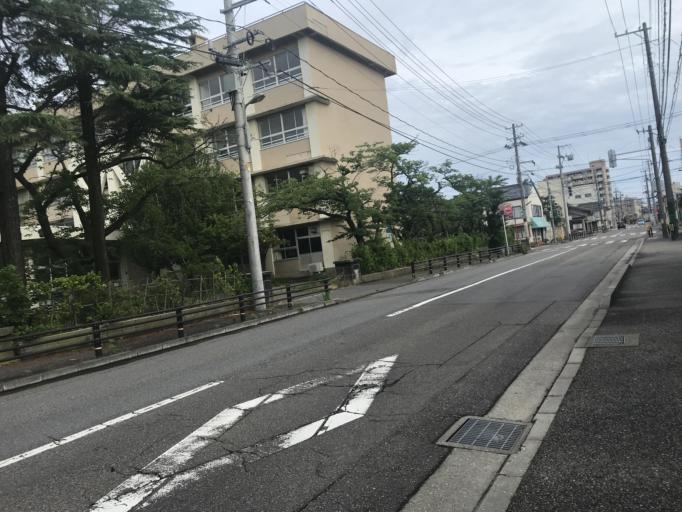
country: JP
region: Niigata
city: Niigata-shi
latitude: 37.9272
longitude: 139.0535
